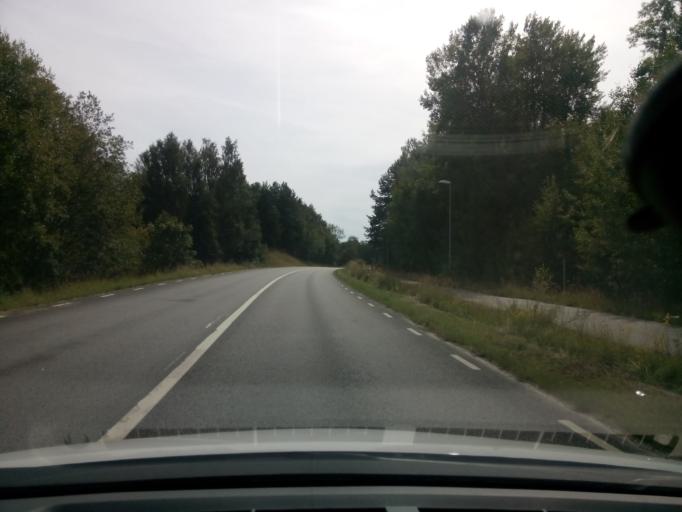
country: SE
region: Soedermanland
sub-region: Nykopings Kommun
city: Nykoping
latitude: 58.7707
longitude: 17.0710
